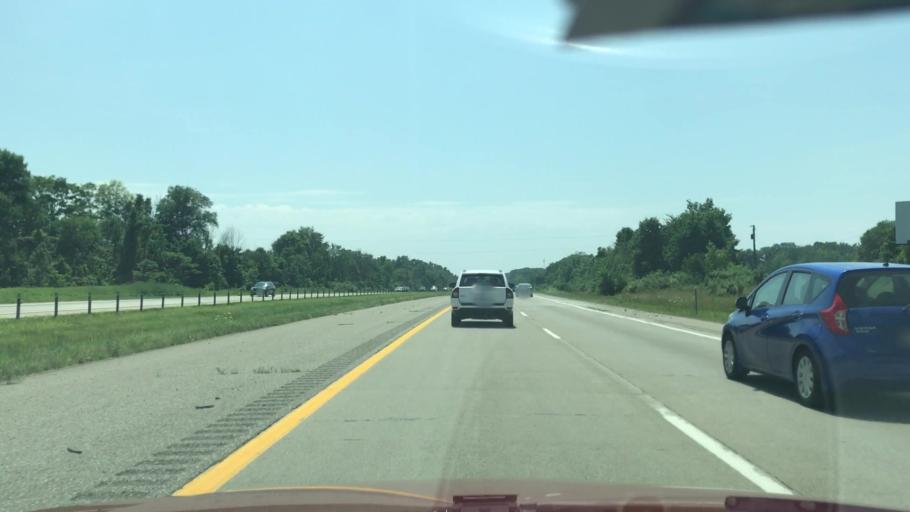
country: US
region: Michigan
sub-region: Berrien County
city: Benton Heights
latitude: 42.1450
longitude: -86.3535
